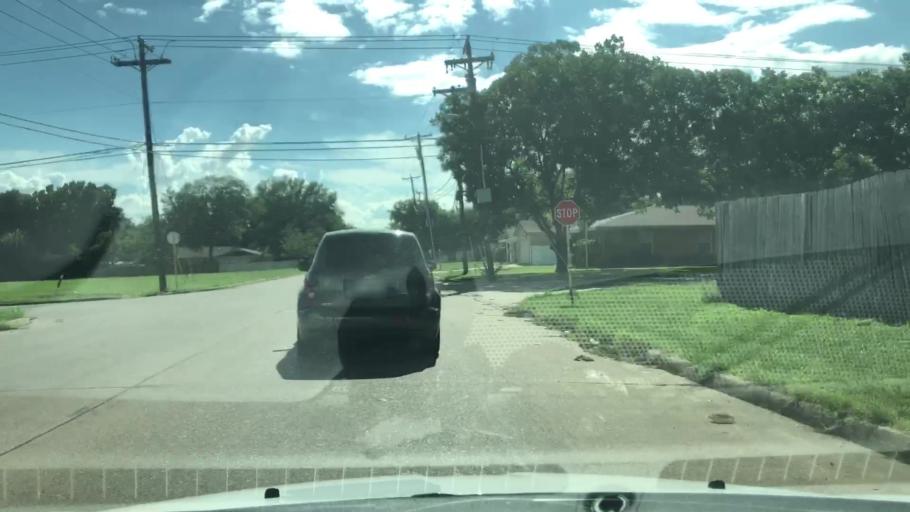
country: US
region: Texas
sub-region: Ellis County
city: Ennis
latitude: 32.3493
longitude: -96.6466
